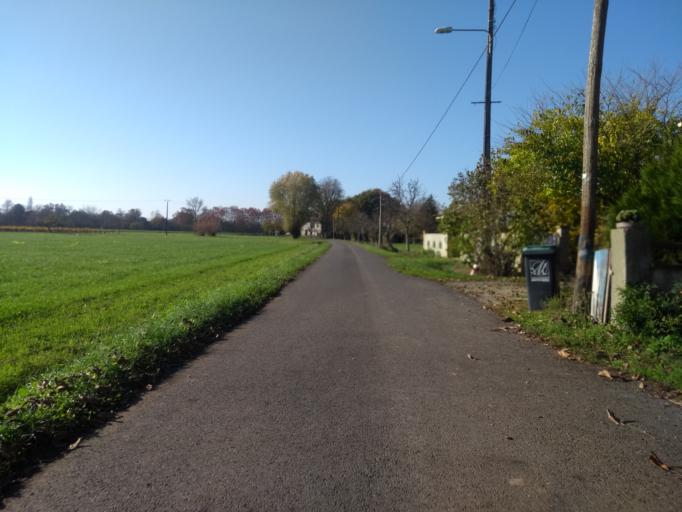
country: FR
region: Aquitaine
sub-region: Departement de la Gironde
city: Cambes
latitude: 44.7311
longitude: -0.4820
